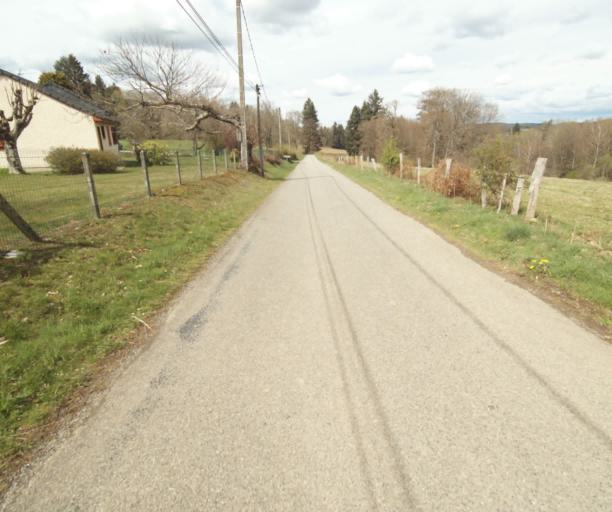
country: FR
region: Limousin
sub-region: Departement de la Correze
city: Laguenne
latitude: 45.2323
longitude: 1.8687
